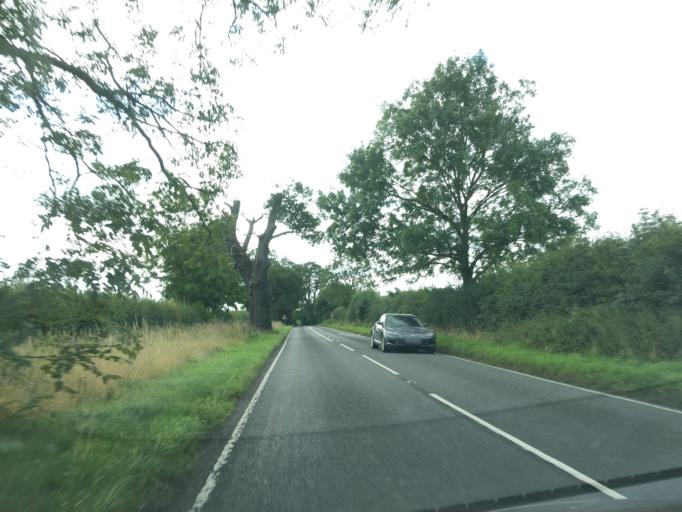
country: GB
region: England
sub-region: Warwickshire
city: Royal Leamington Spa
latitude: 52.3328
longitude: -1.5221
